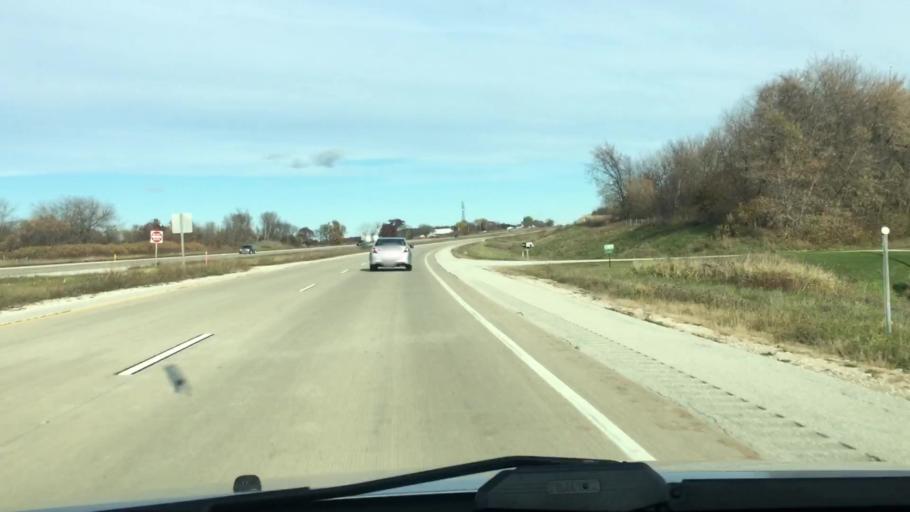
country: US
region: Wisconsin
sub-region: Kewaunee County
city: Luxemburg
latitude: 44.7057
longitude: -87.7044
